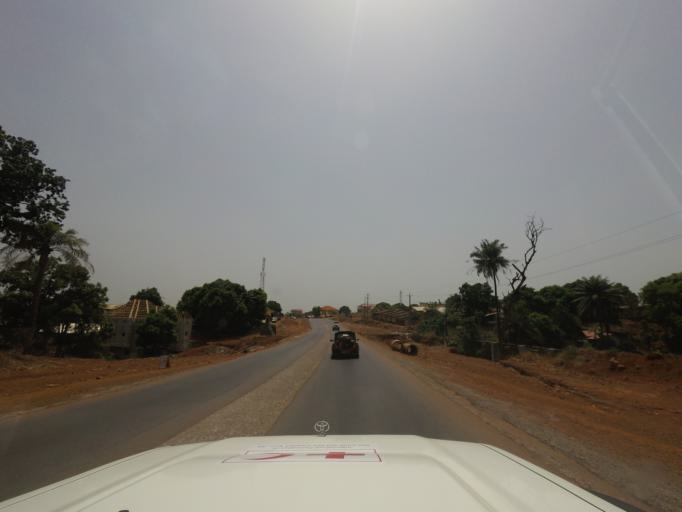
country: GN
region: Kindia
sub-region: Coyah
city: Coyah
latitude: 9.7255
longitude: -13.4557
